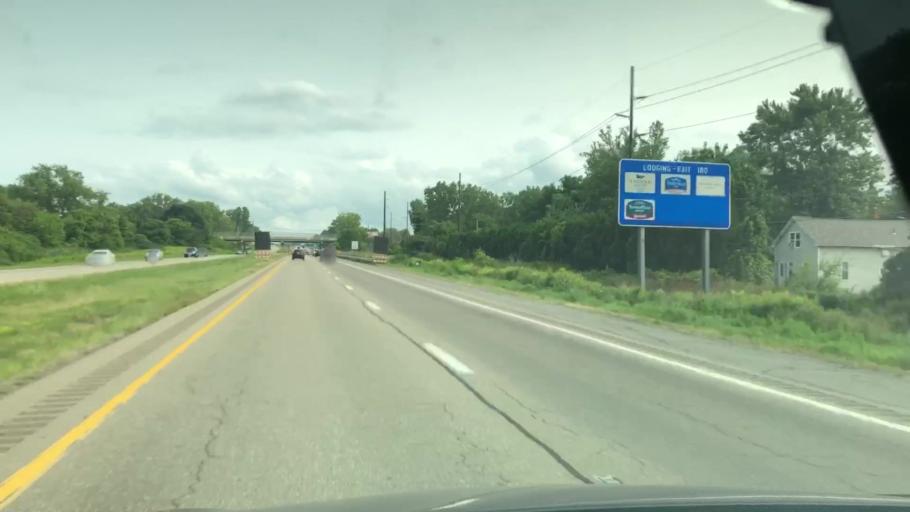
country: US
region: Pennsylvania
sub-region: Erie County
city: Erie
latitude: 42.0872
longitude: -80.1174
